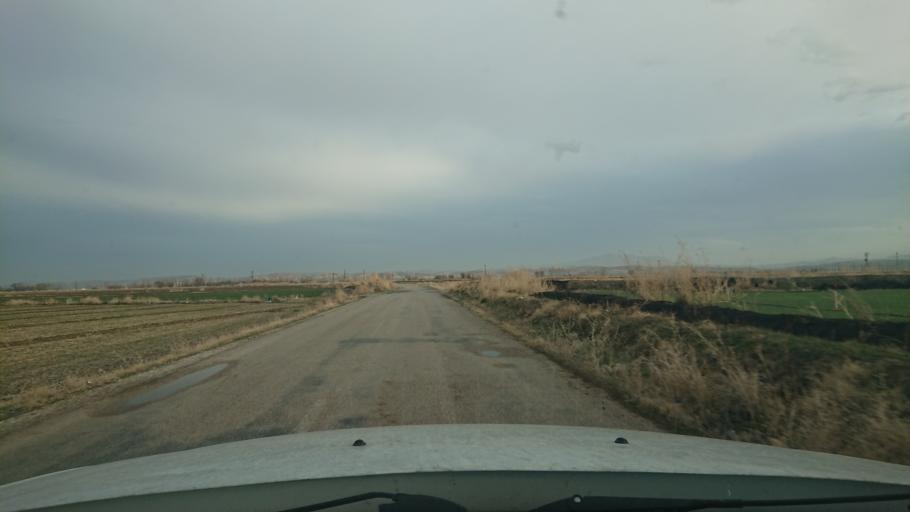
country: TR
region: Aksaray
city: Yesilova
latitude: 38.4344
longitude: 33.8374
